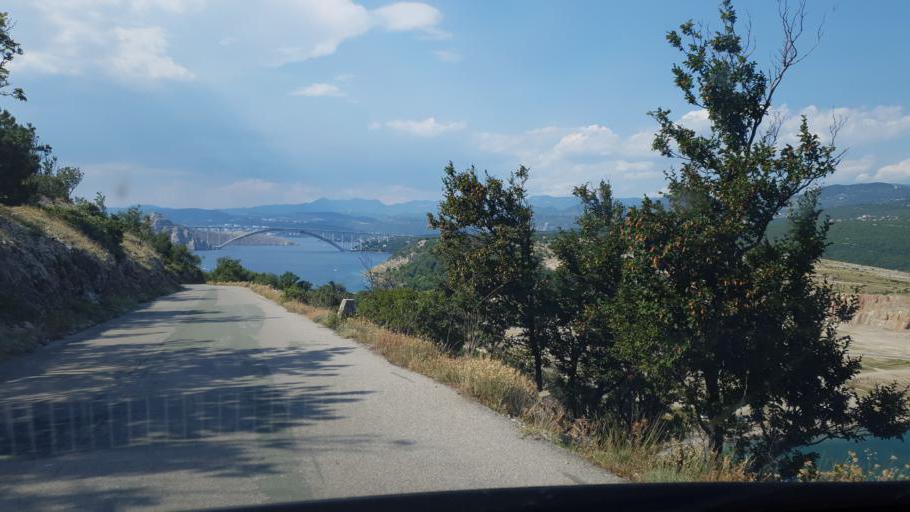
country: HR
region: Primorsko-Goranska
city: Omisalj
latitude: 45.2286
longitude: 14.5814
